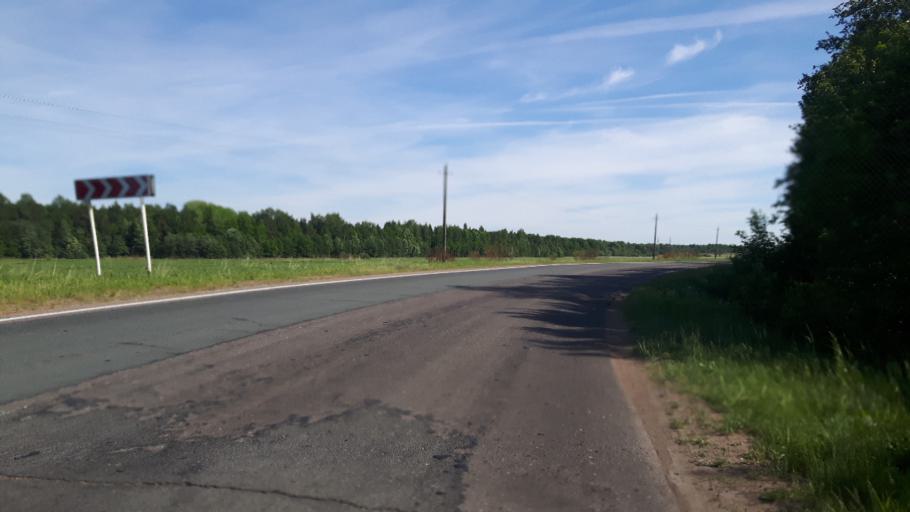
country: RU
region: Leningrad
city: Ivangorod
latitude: 59.4120
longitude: 28.3842
